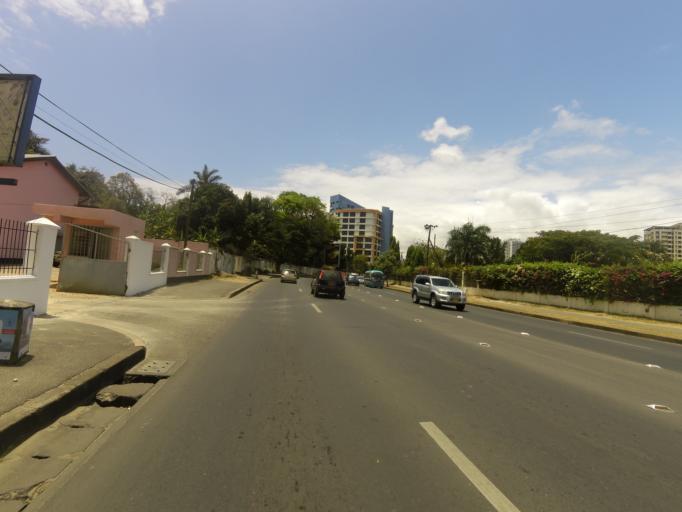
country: TZ
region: Dar es Salaam
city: Dar es Salaam
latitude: -6.8026
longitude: 39.2856
